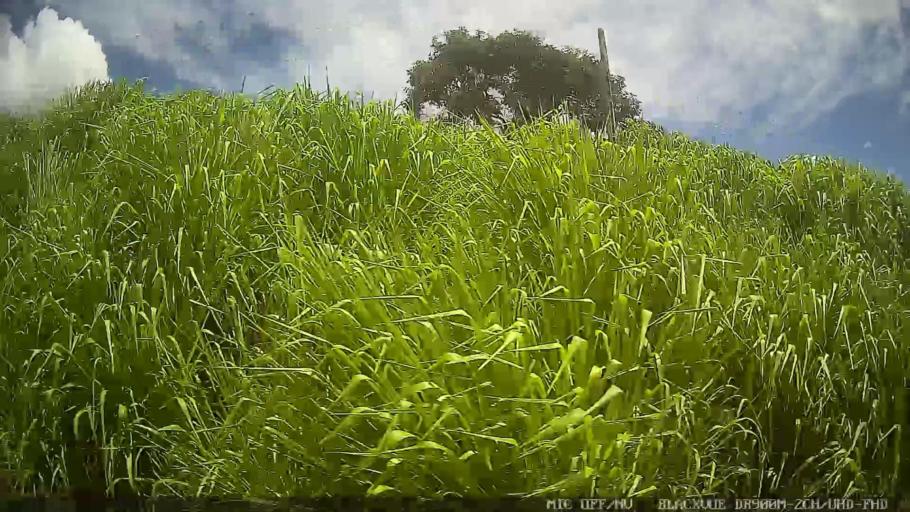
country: BR
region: Minas Gerais
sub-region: Extrema
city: Extrema
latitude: -22.7250
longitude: -46.3995
